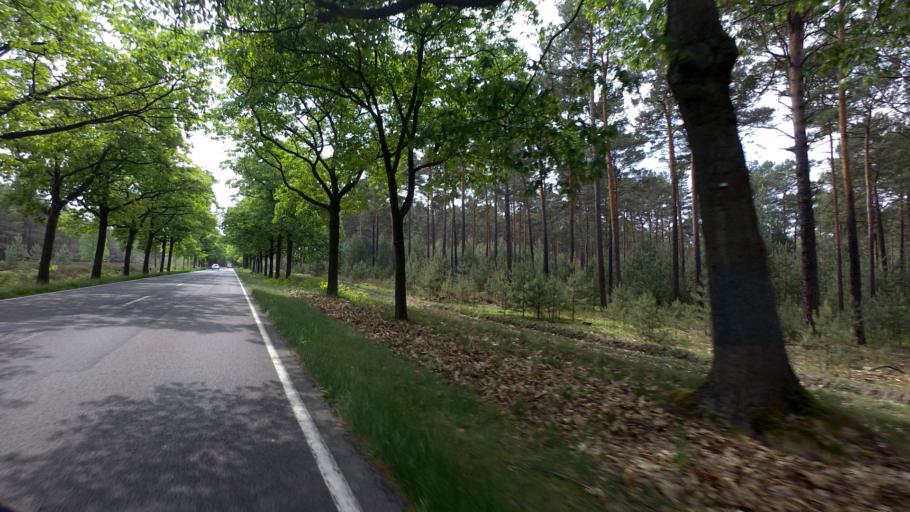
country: DE
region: Brandenburg
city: Drachhausen
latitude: 51.9051
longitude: 14.3546
